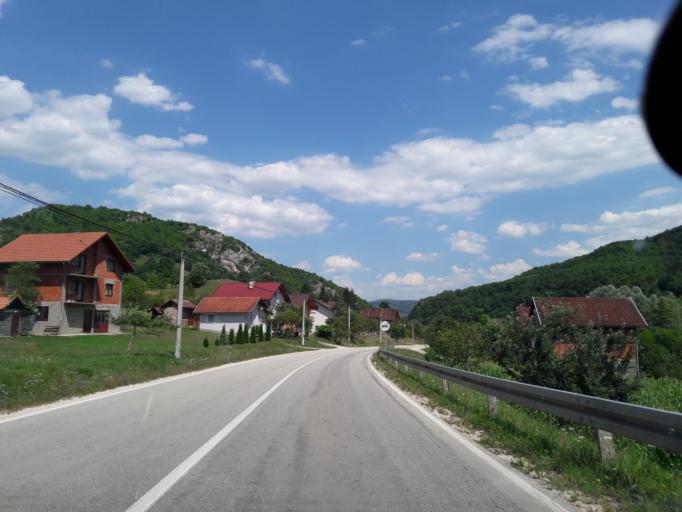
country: BA
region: Republika Srpska
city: Mrkonjic Grad
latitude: 44.4215
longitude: 17.1147
